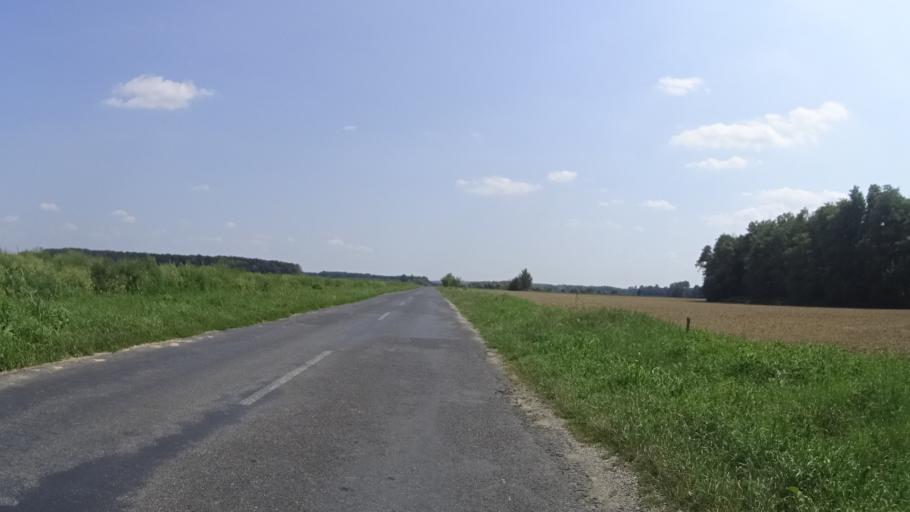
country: HU
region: Zala
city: Murakeresztur
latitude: 46.3766
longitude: 16.8485
